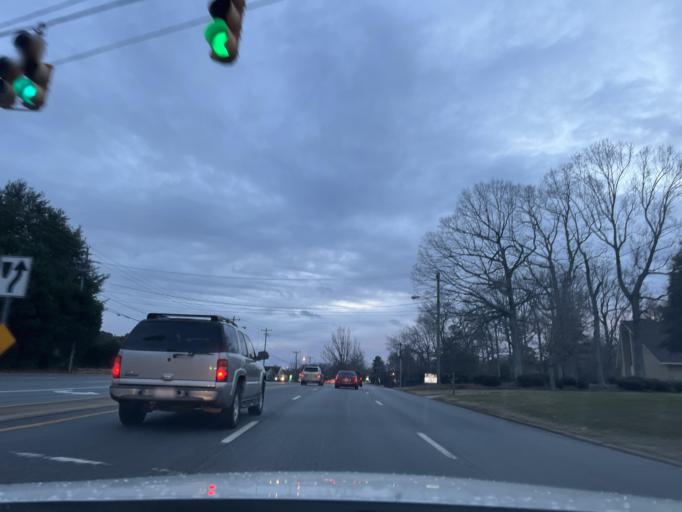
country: US
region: North Carolina
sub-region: Guilford County
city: Greensboro
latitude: 36.0245
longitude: -79.8469
